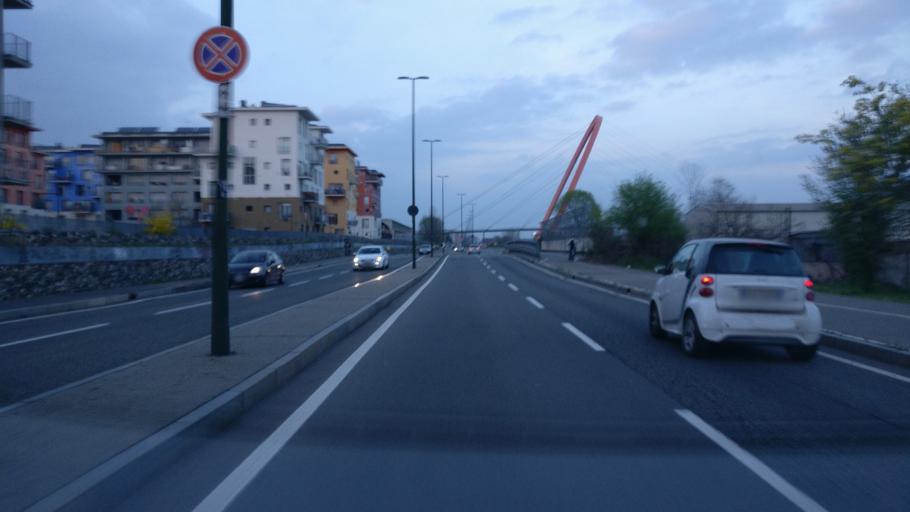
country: IT
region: Piedmont
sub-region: Provincia di Torino
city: Nichelino
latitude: 45.0289
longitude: 7.6562
